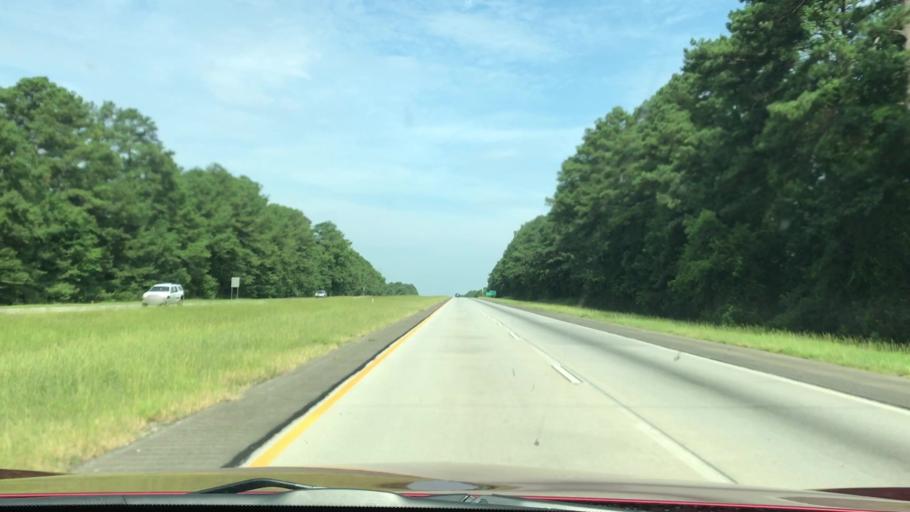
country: US
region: Georgia
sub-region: Warren County
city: Firing Range
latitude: 33.5002
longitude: -82.7031
